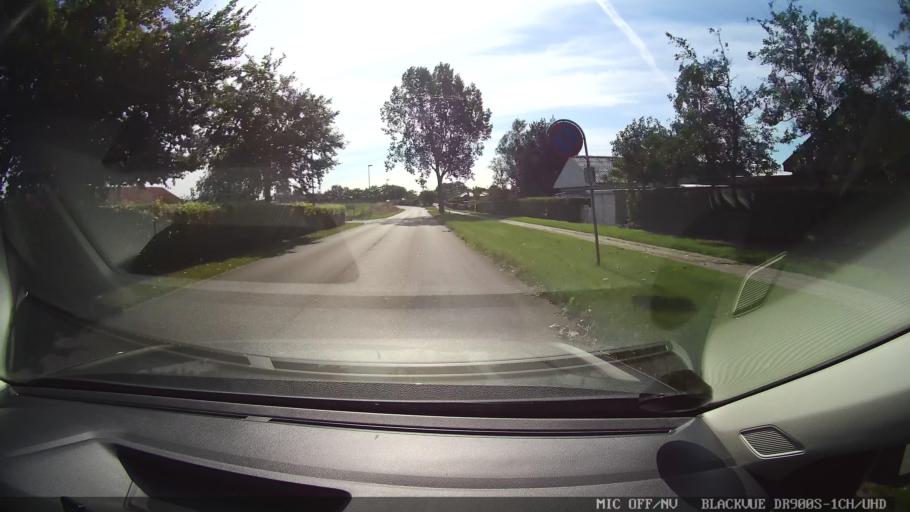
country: DK
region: North Denmark
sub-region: Mariagerfjord Kommune
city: Hobro
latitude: 56.5463
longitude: 9.8536
